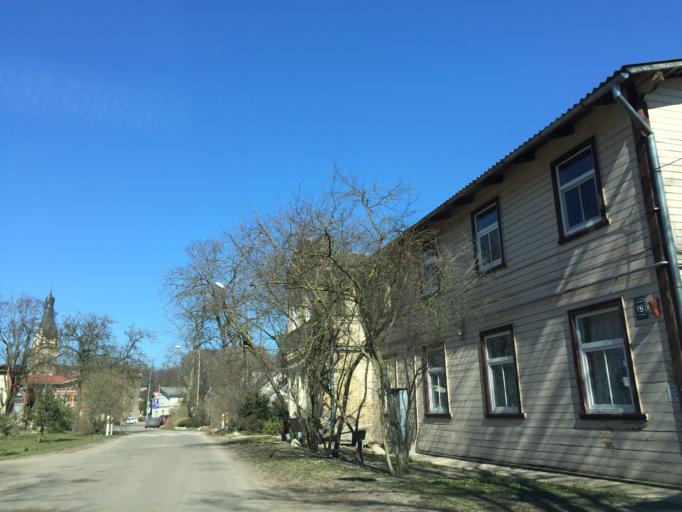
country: LV
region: Jurmala
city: Jurmala
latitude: 56.9675
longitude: 23.7736
